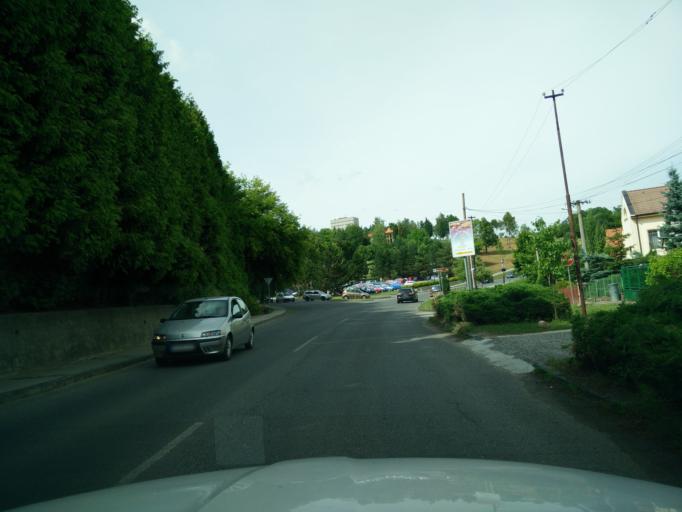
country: SK
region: Nitriansky
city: Bojnice
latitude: 48.7704
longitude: 18.5743
